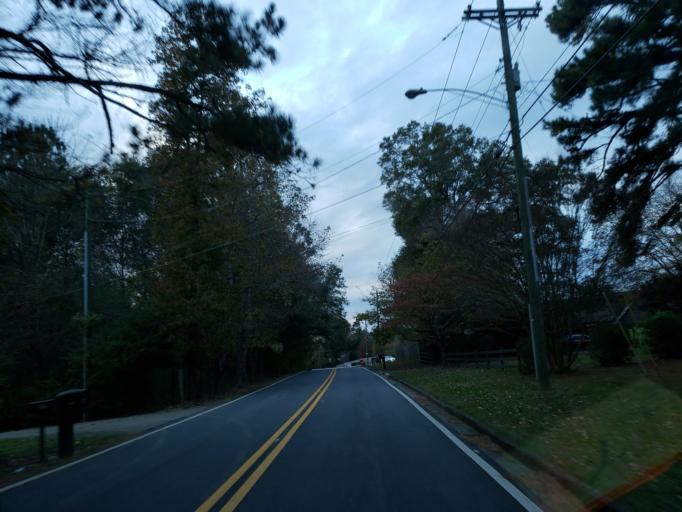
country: US
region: Georgia
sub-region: Cobb County
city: Acworth
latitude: 34.0313
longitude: -84.6864
